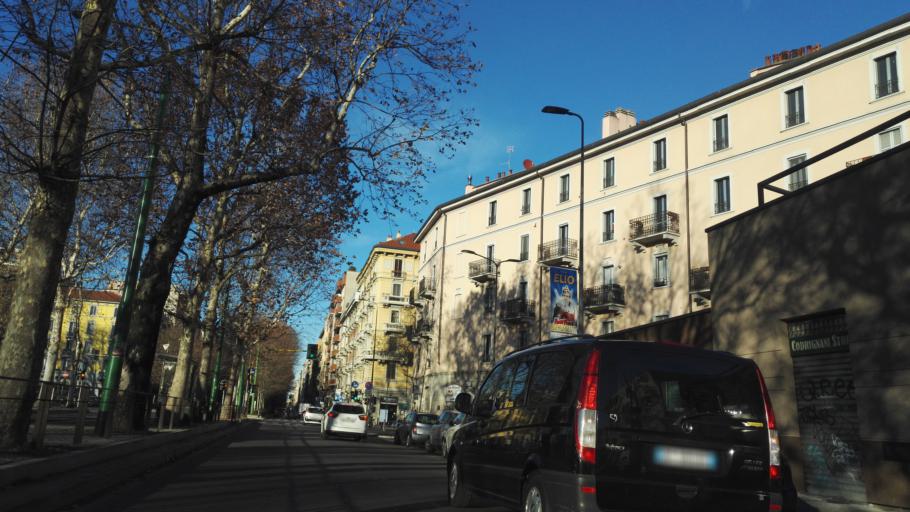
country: IT
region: Lombardy
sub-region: Citta metropolitana di Milano
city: Milano
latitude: 45.4614
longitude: 9.2175
